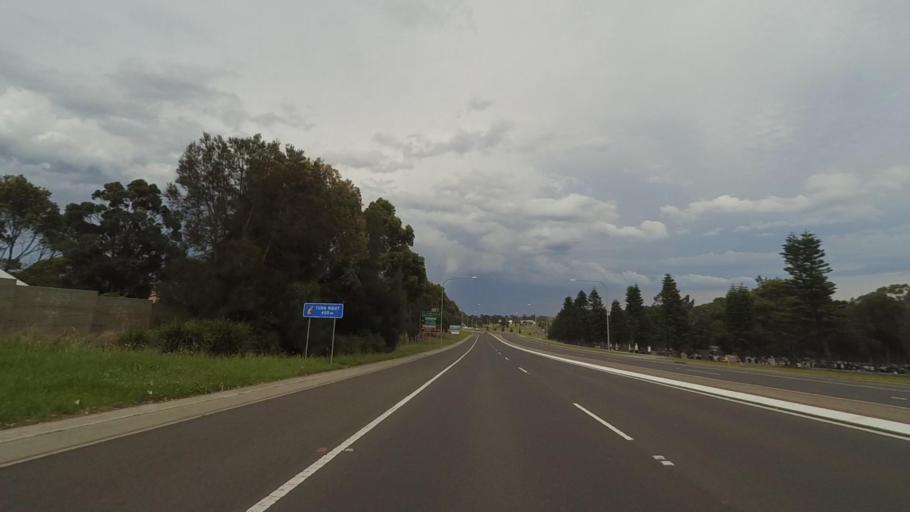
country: AU
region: New South Wales
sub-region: Shellharbour
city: Flinders
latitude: -34.5839
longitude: 150.8577
